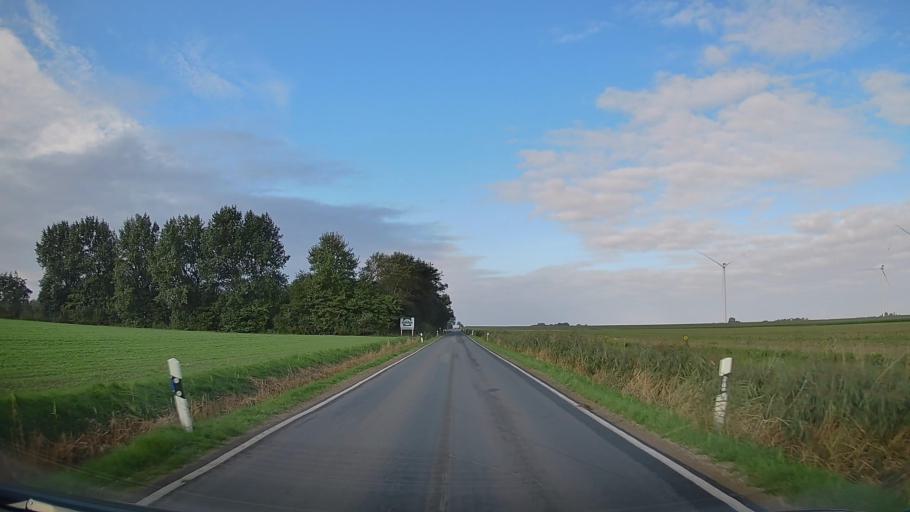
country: DE
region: Schleswig-Holstein
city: Breklum
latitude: 54.5724
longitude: 8.9505
